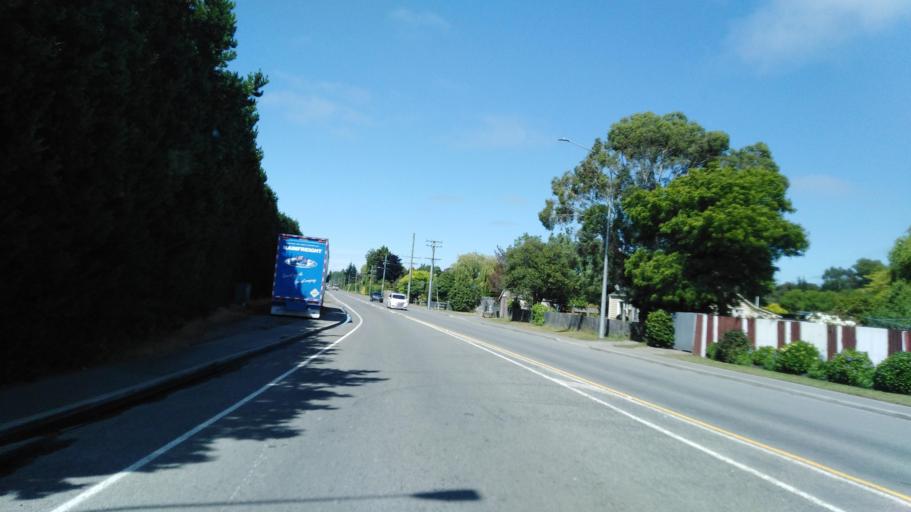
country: NZ
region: Canterbury
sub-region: Selwyn District
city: Prebbleton
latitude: -43.5130
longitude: 172.5087
